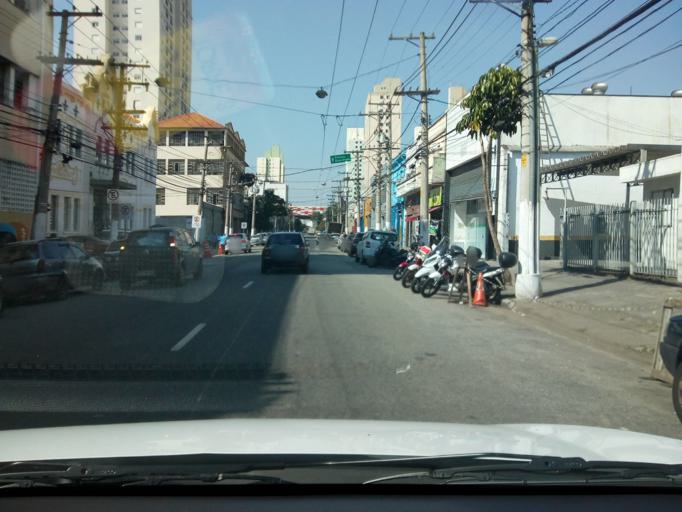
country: BR
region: Sao Paulo
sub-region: Sao Paulo
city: Sao Paulo
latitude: -23.5458
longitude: -46.6206
